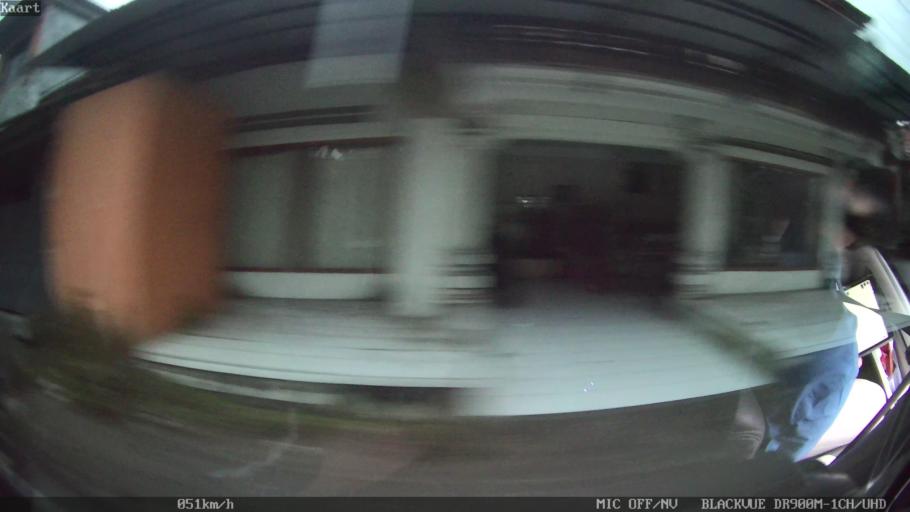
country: ID
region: Bali
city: Bayad
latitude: -8.4477
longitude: 115.2423
